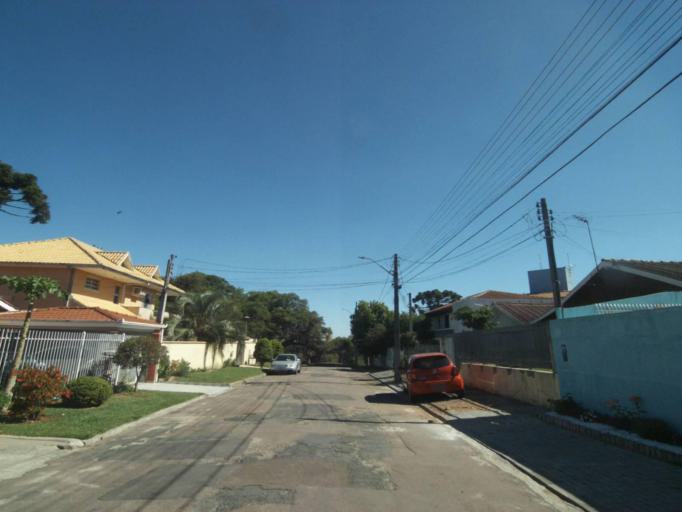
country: BR
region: Parana
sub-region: Curitiba
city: Curitiba
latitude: -25.4556
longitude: -49.3515
